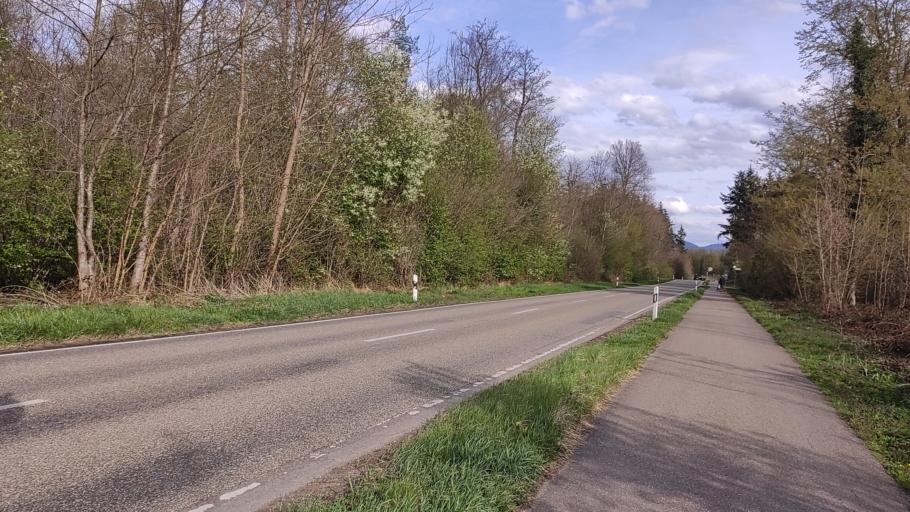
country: DE
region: Baden-Wuerttemberg
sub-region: Freiburg Region
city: Umkirch
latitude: 47.9968
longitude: 7.7690
